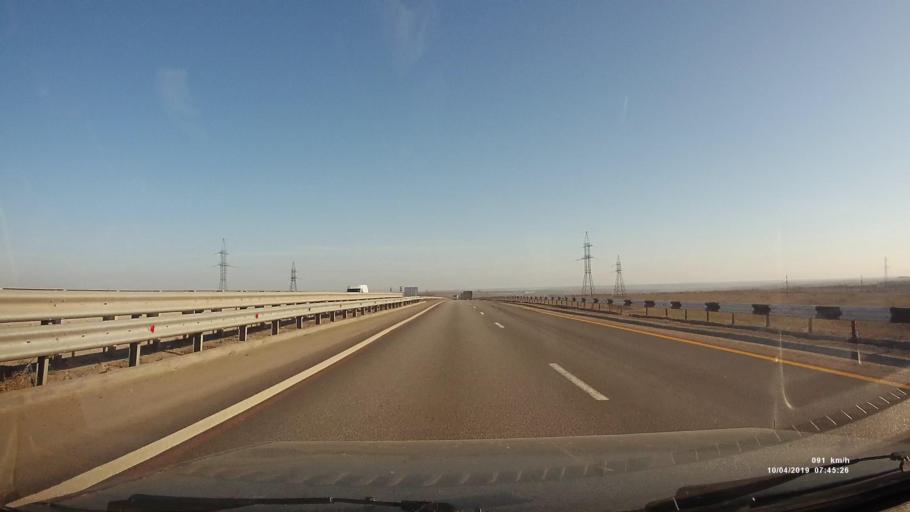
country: RU
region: Rostov
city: Likhoy
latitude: 48.1914
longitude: 40.2665
